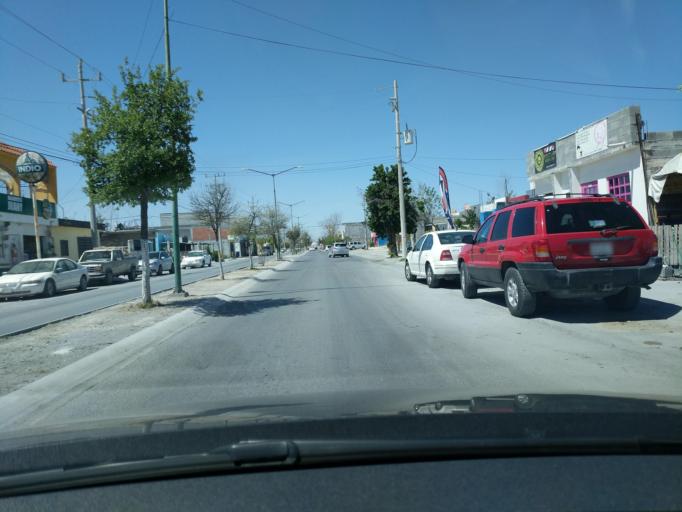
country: MX
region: Nuevo Leon
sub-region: Pesqueria
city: Colinas del Aeropuerto
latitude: 25.8241
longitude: -100.1180
